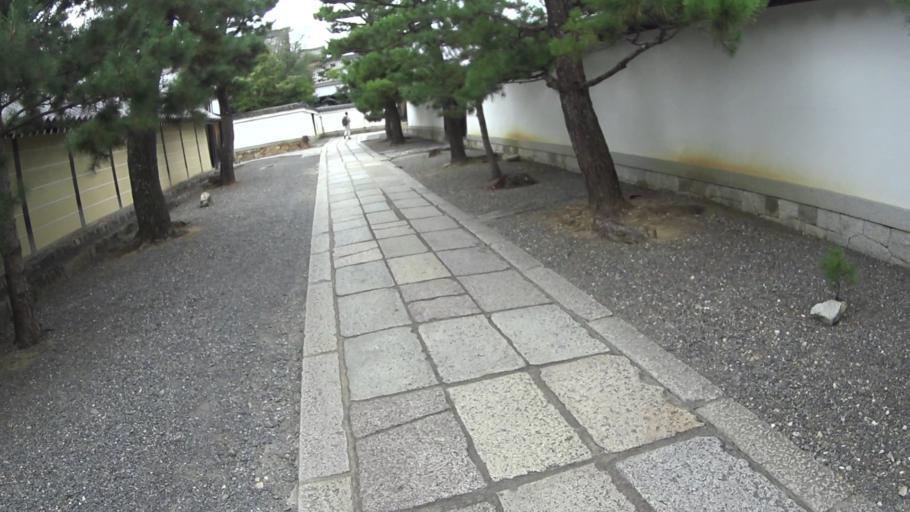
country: JP
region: Kyoto
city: Kyoto
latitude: 35.0233
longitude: 135.7197
